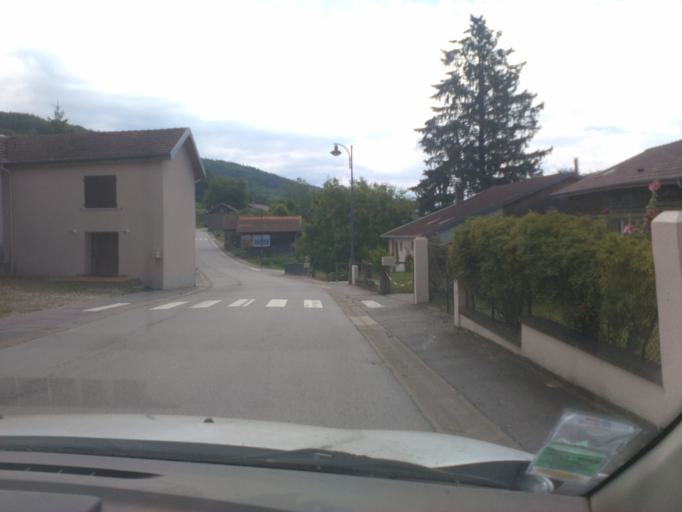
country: FR
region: Lorraine
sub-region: Departement des Vosges
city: Bruyeres
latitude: 48.1396
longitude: 6.6950
